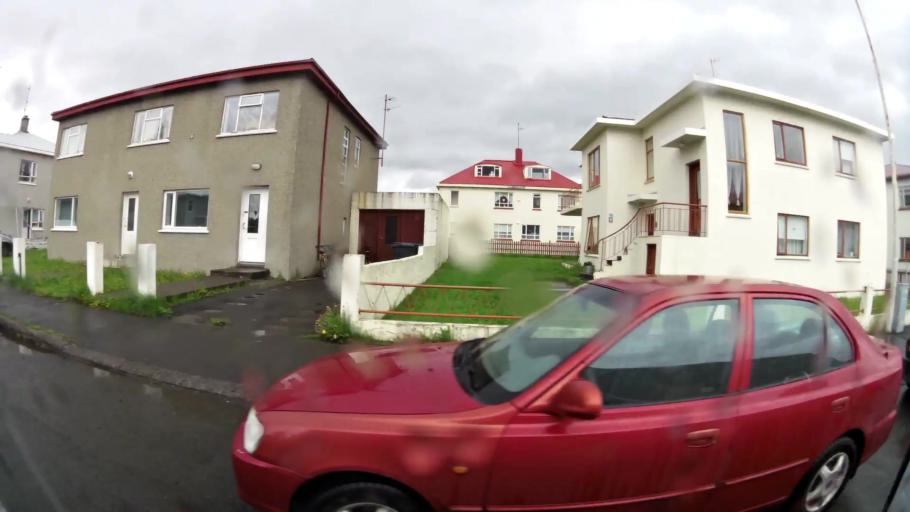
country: IS
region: Northeast
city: Akureyri
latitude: 65.6892
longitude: -18.0901
